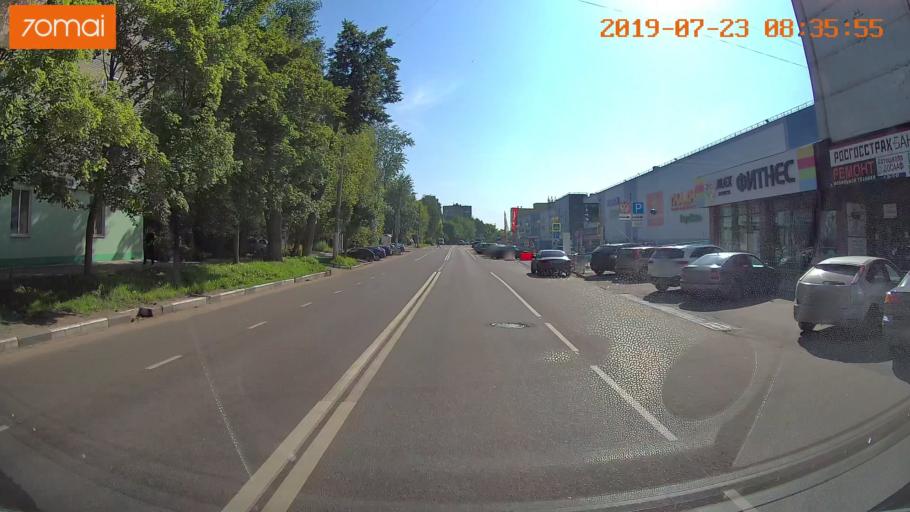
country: RU
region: Ivanovo
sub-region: Gorod Ivanovo
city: Ivanovo
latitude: 57.0060
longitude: 40.9822
